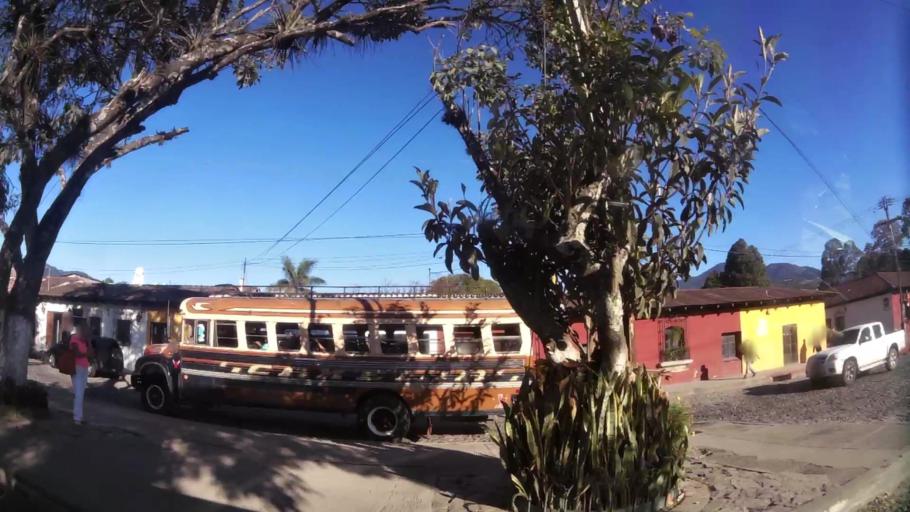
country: GT
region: Sacatepequez
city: Antigua Guatemala
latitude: 14.5545
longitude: -90.7380
